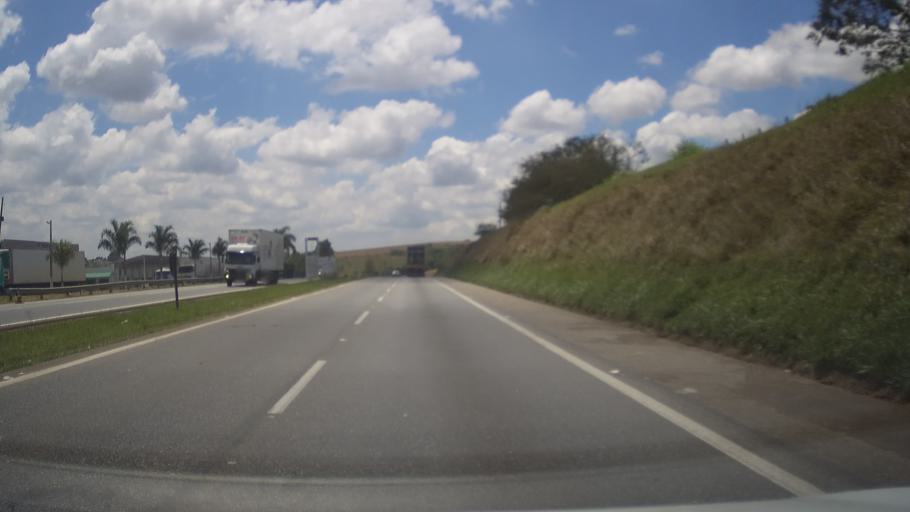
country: BR
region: Minas Gerais
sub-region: Campanha
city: Campanha
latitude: -21.7986
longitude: -45.4606
